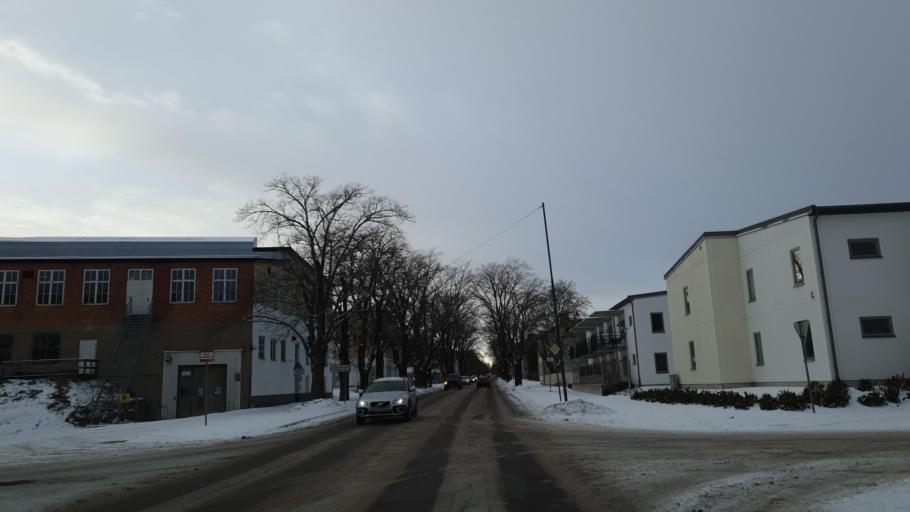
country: SE
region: Gaevleborg
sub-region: Soderhamns Kommun
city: Soderhamn
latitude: 61.3079
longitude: 17.0676
